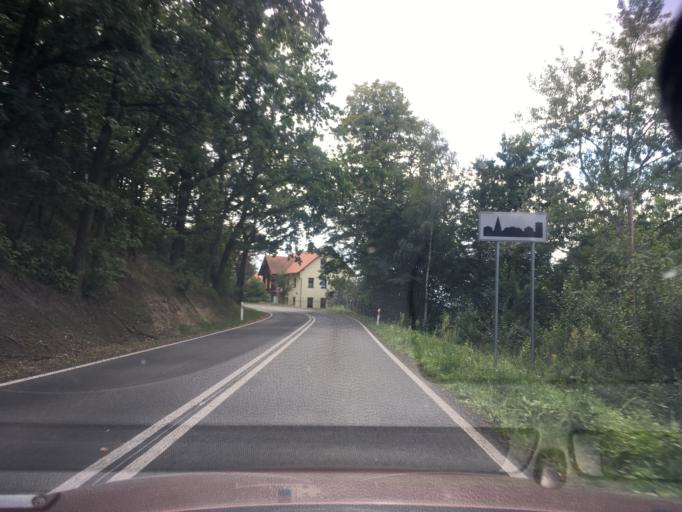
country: PL
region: Lower Silesian Voivodeship
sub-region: Powiat zgorzelecki
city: Lagow
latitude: 51.2036
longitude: 15.0200
